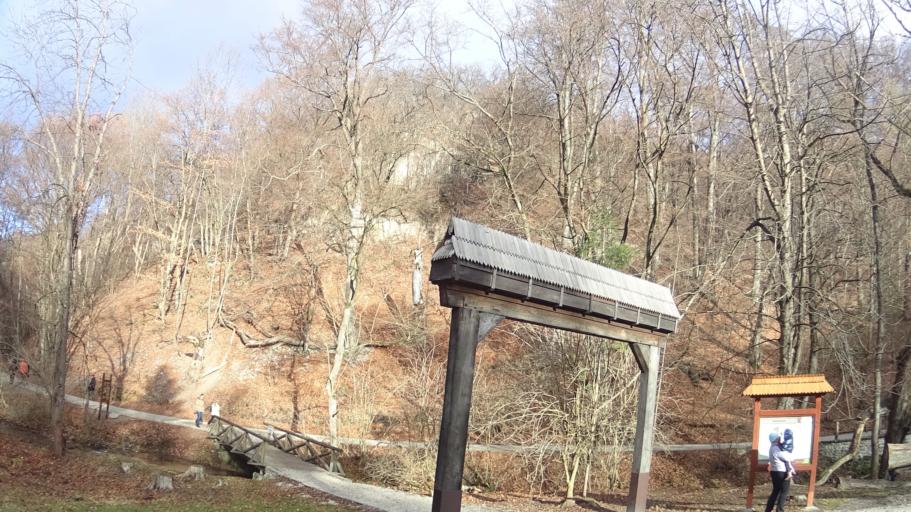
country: HU
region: Heves
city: Szilvasvarad
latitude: 48.0767
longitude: 20.4084
